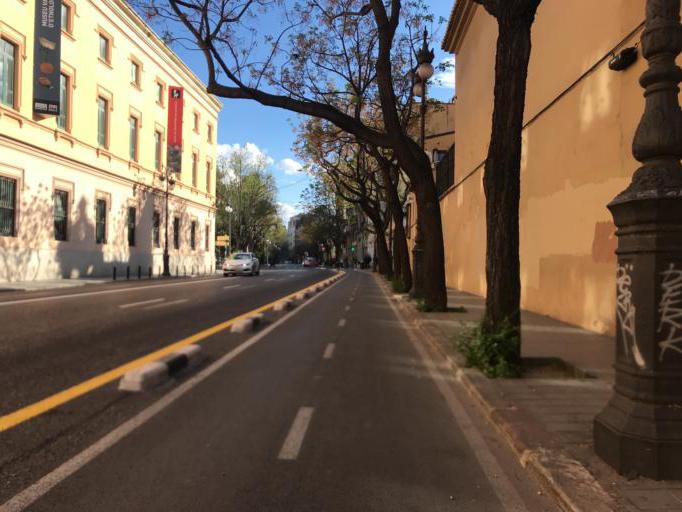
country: ES
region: Valencia
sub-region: Provincia de Valencia
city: Valencia
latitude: 39.4789
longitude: -0.3832
